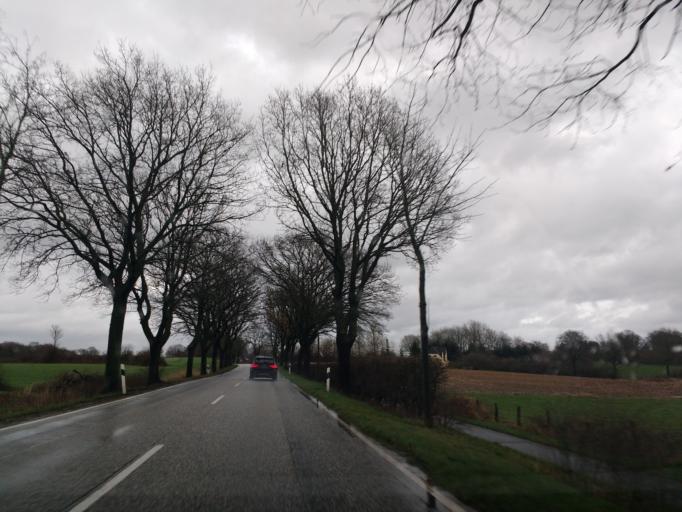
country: DE
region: Schleswig-Holstein
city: Blekendorf
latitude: 54.2855
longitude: 10.7009
